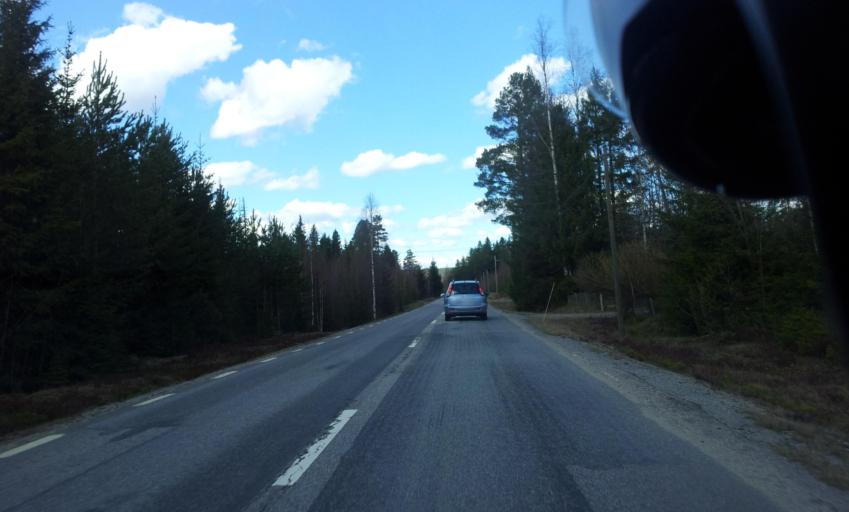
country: SE
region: Gaevleborg
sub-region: Ovanakers Kommun
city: Edsbyn
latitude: 61.3046
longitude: 15.8875
